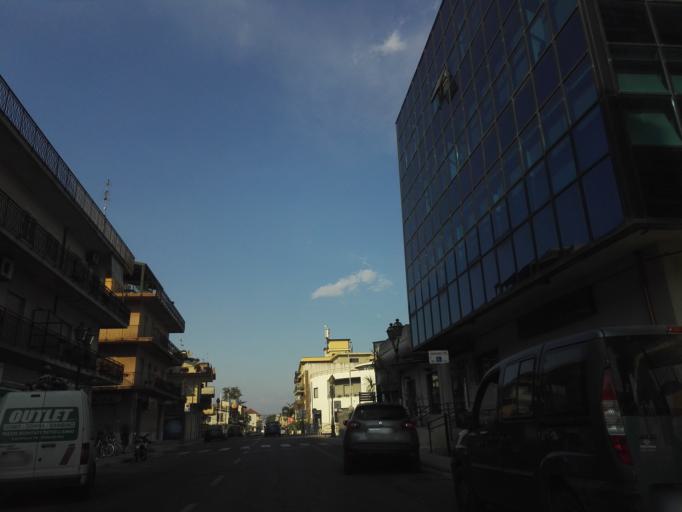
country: IT
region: Calabria
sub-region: Provincia di Reggio Calabria
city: Siderno
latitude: 38.2723
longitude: 16.3025
